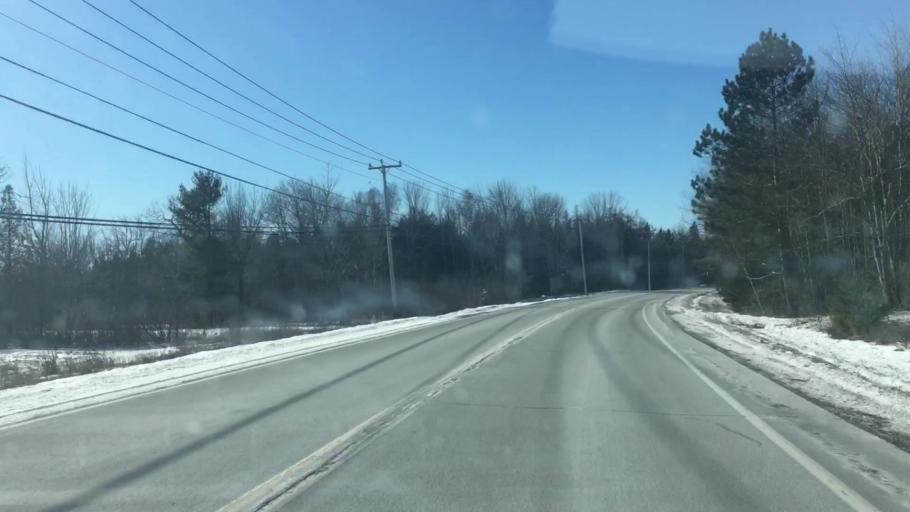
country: US
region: Maine
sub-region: Hancock County
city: Surry
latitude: 44.4949
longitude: -68.4472
